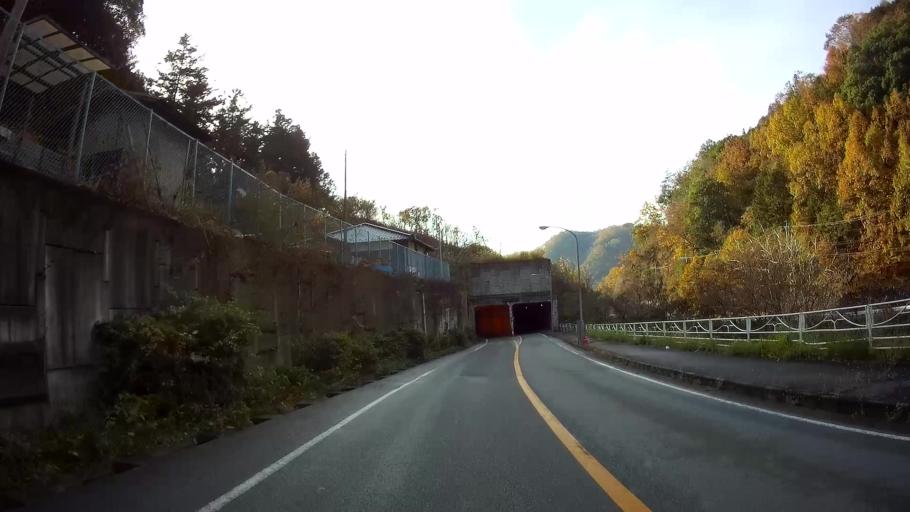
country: JP
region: Yamanashi
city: Fujikawaguchiko
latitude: 35.4737
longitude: 138.5339
